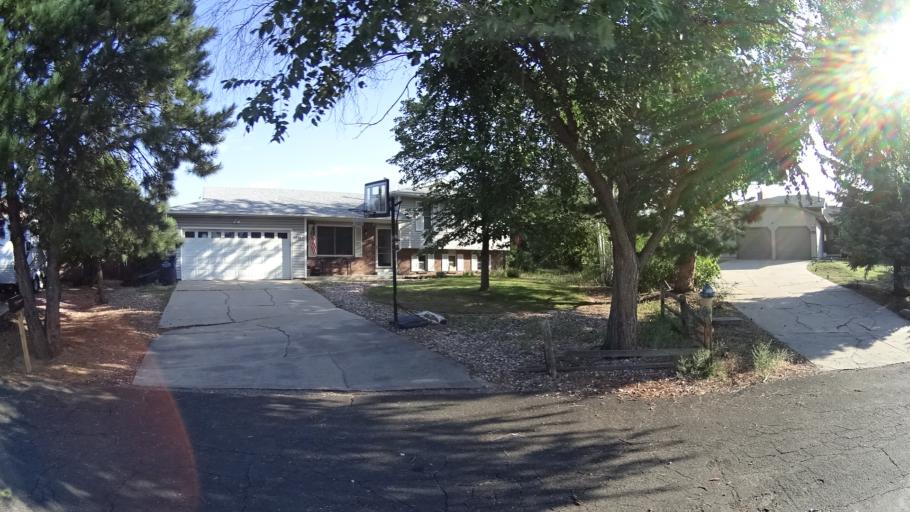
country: US
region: Colorado
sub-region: El Paso County
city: Air Force Academy
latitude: 38.9463
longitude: -104.7850
